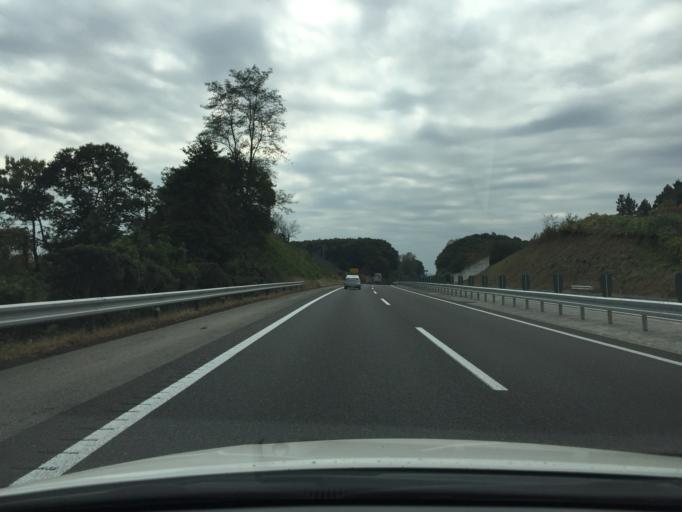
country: JP
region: Fukushima
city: Sukagawa
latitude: 37.2328
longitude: 140.3261
